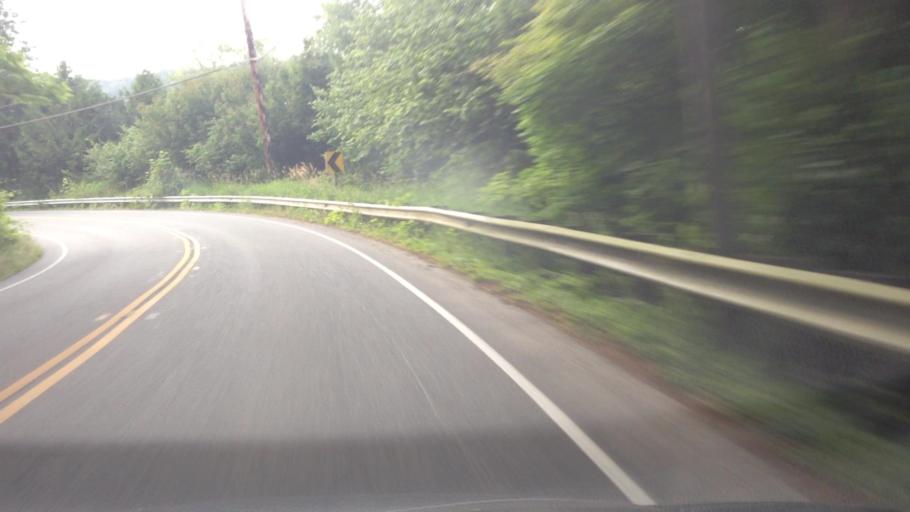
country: US
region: Washington
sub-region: King County
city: Lake Marcel-Stillwater
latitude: 47.7456
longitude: -121.9282
